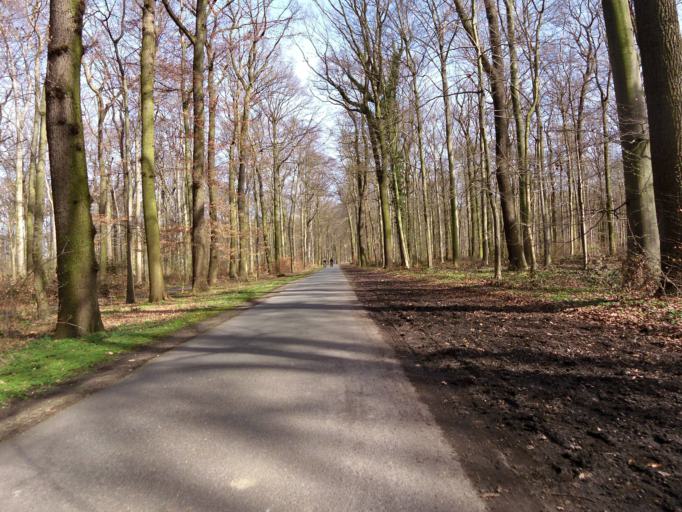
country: DE
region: Lower Saxony
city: Laatzen
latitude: 52.3558
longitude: 9.7799
